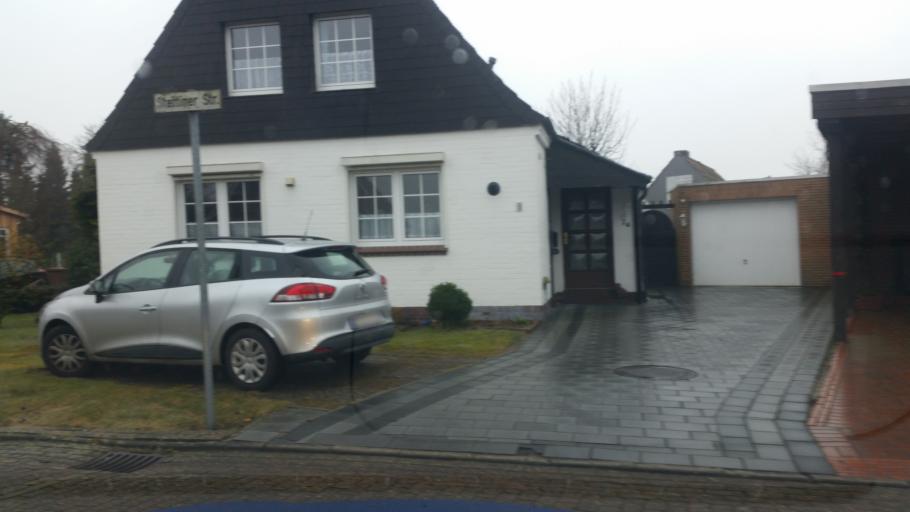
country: DE
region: Lower Saxony
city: Zetel
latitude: 53.4167
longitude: 7.9572
